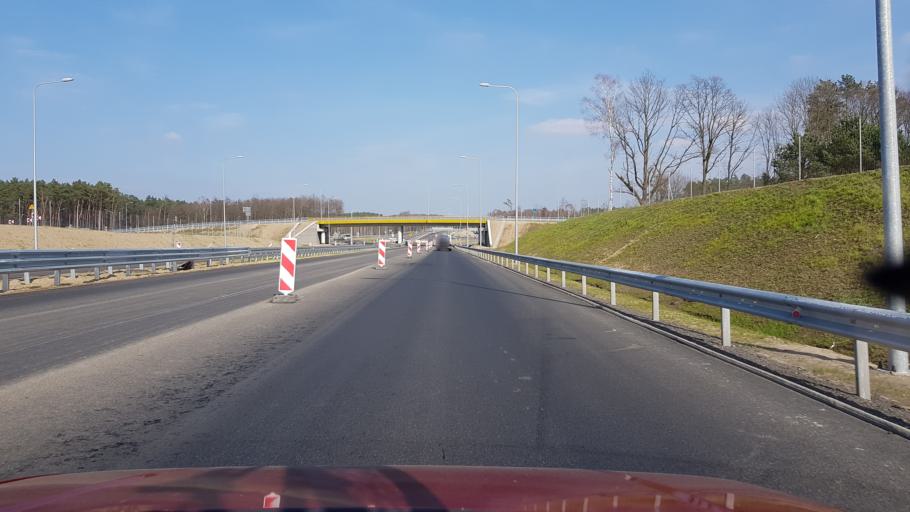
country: PL
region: West Pomeranian Voivodeship
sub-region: Powiat goleniowski
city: Osina
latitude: 53.6308
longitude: 14.9927
